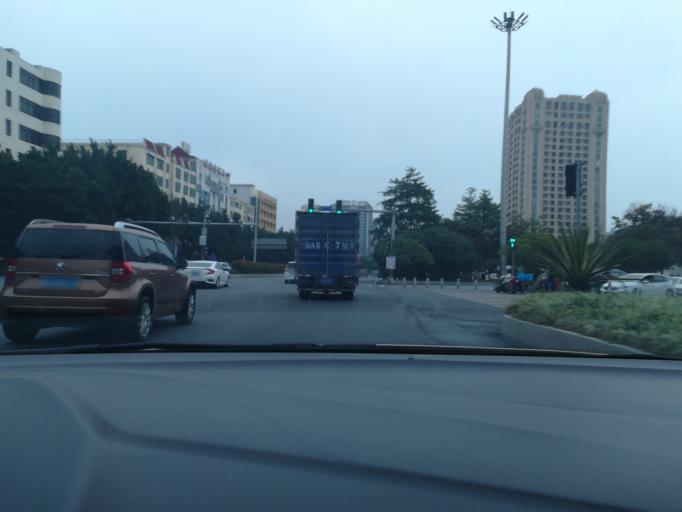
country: CN
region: Guangdong
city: Nansha
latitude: 22.8031
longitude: 113.5449
